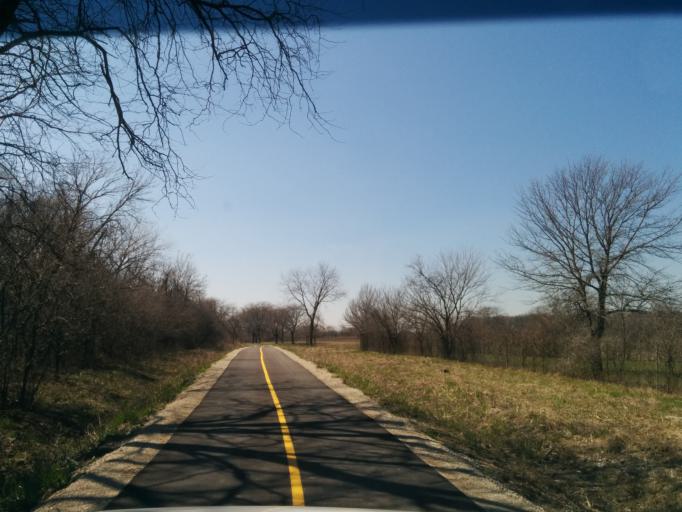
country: US
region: Illinois
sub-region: Cook County
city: Midlothian
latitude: 41.6014
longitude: -87.7187
